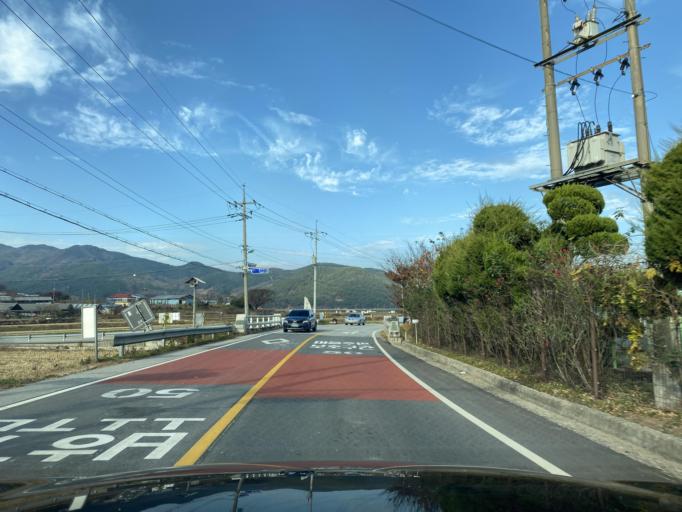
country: KR
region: Chungcheongnam-do
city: Hongsung
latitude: 36.6748
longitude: 126.6425
